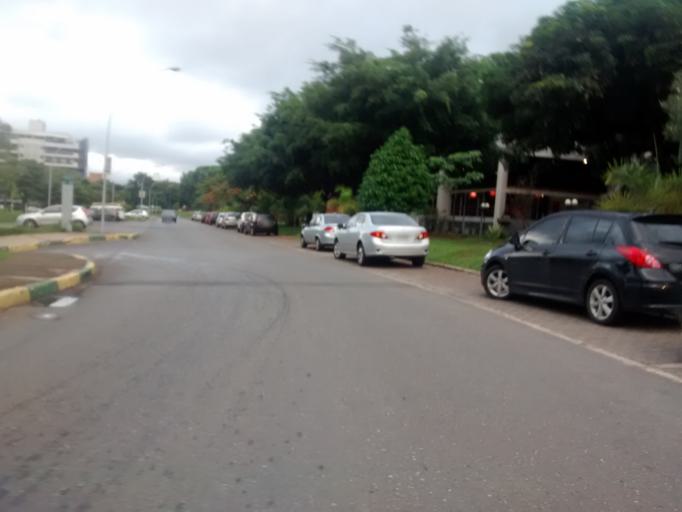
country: BR
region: Federal District
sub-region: Brasilia
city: Brasilia
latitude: -15.7586
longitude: -47.8886
